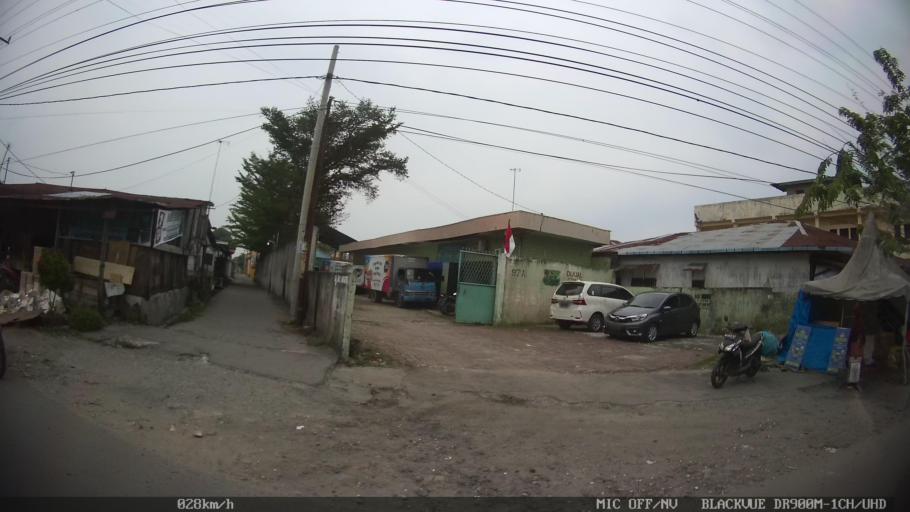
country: ID
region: North Sumatra
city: Medan
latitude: 3.5620
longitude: 98.7207
